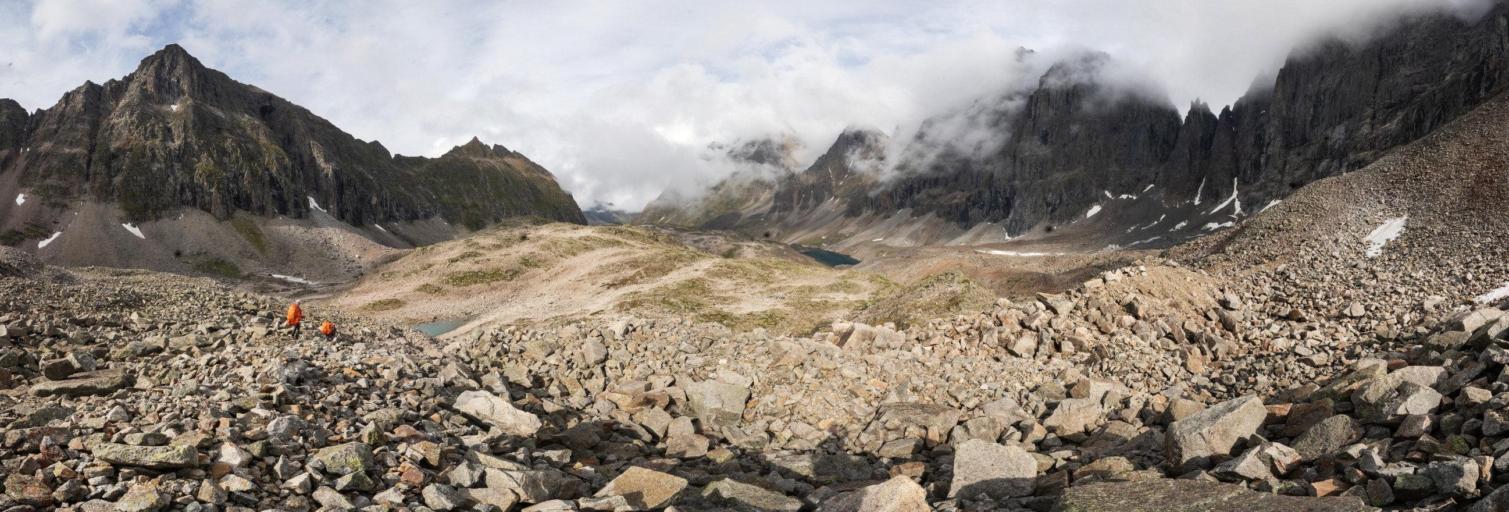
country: RU
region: Transbaikal Territory
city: Chara
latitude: 56.9844
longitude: 117.6600
